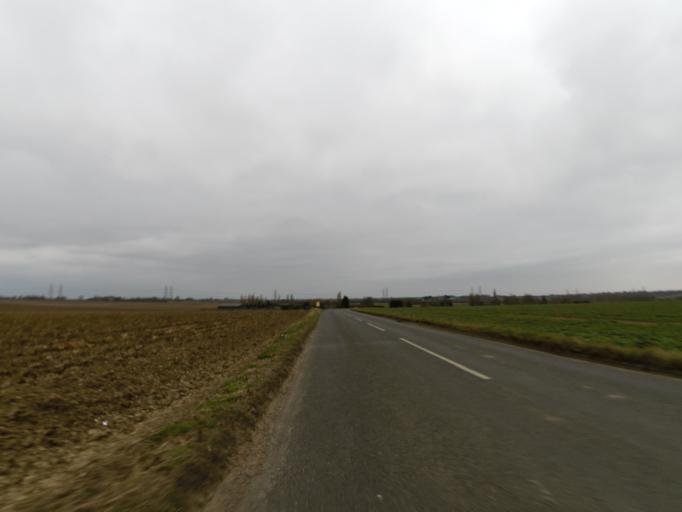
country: GB
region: England
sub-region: Suffolk
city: Ipswich
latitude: 52.1062
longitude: 1.1531
